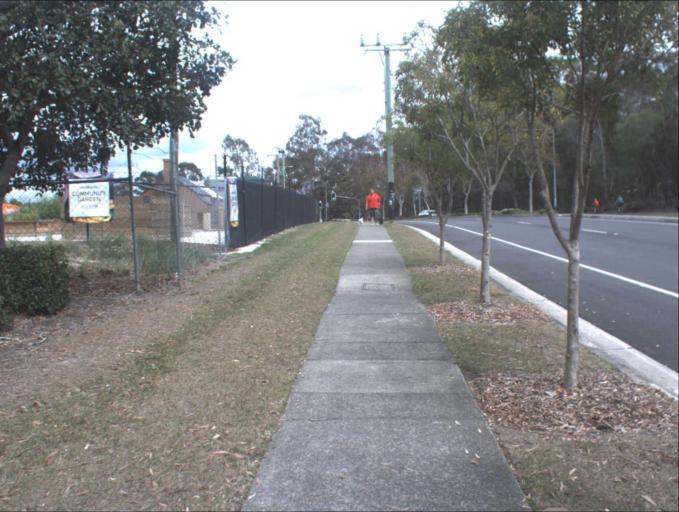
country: AU
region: Queensland
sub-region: Logan
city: Slacks Creek
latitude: -27.6553
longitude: 153.1703
